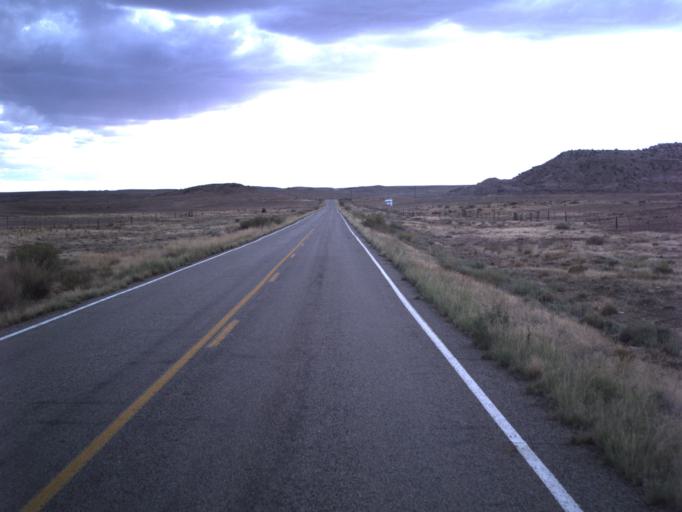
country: US
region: Utah
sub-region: San Juan County
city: Blanding
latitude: 37.4278
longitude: -109.4114
